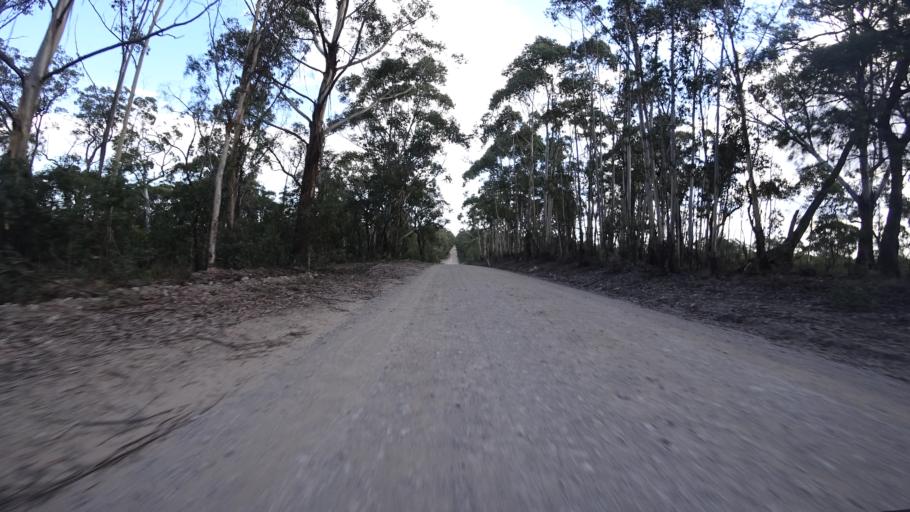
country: AU
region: New South Wales
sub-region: Lithgow
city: Lithgow
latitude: -33.4204
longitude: 150.2033
